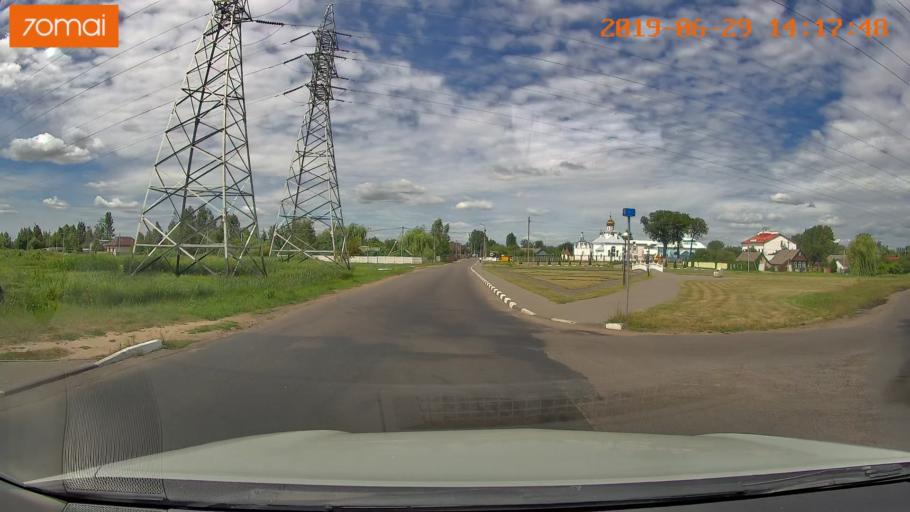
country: BY
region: Minsk
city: Salihorsk
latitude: 52.8004
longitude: 27.5401
